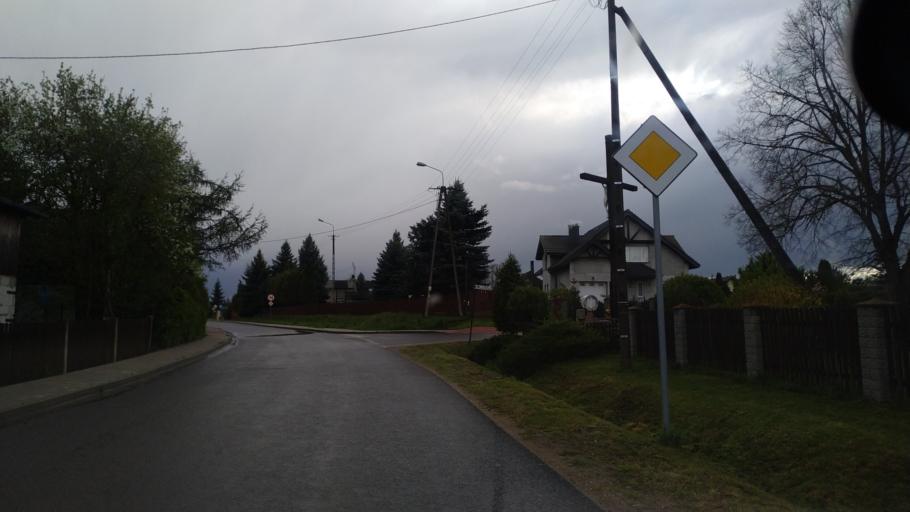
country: PL
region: Pomeranian Voivodeship
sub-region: Powiat starogardzki
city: Osiek
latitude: 53.6382
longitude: 18.4810
